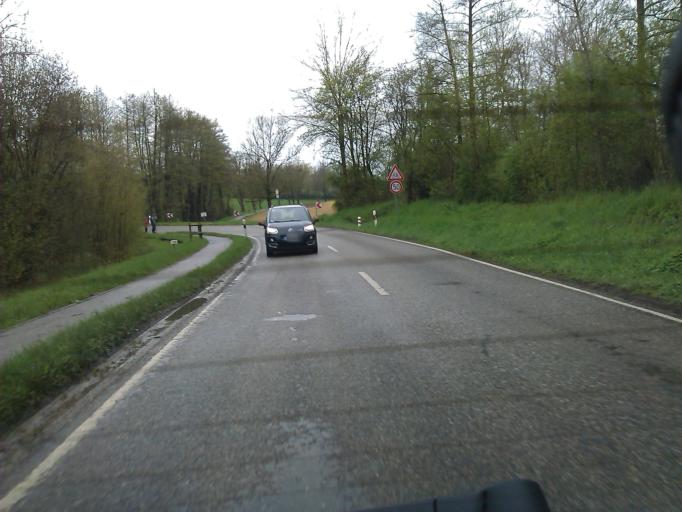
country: DE
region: Baden-Wuerttemberg
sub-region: Regierungsbezirk Stuttgart
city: Bad Wimpfen
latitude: 49.2371
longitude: 9.1455
